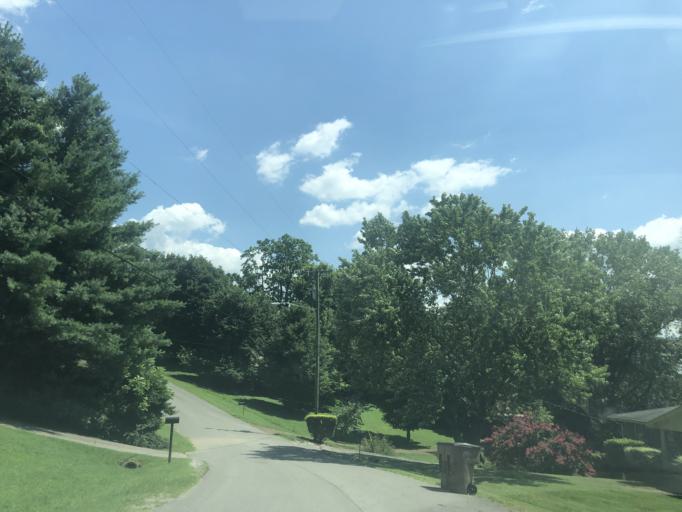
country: US
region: Tennessee
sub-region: Davidson County
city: Nashville
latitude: 36.1845
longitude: -86.7135
